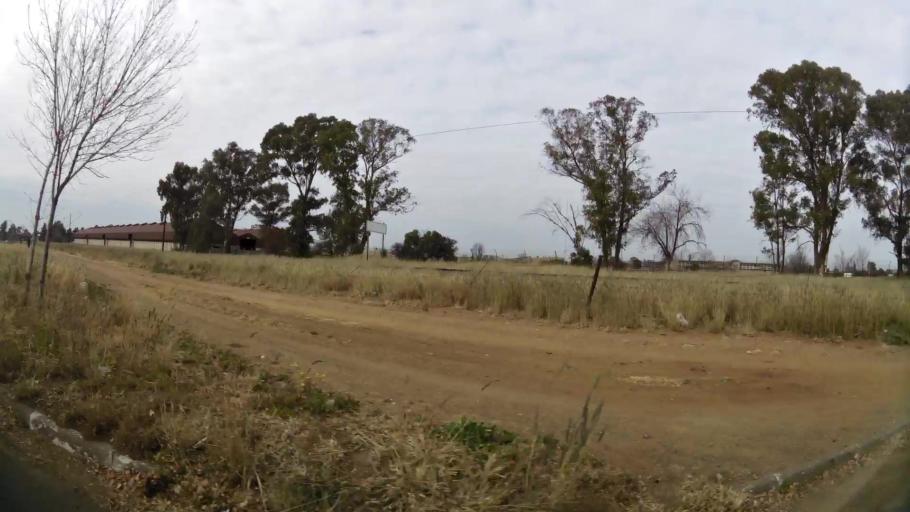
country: ZA
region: Orange Free State
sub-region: Mangaung Metropolitan Municipality
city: Bloemfontein
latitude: -29.1327
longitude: 26.2020
